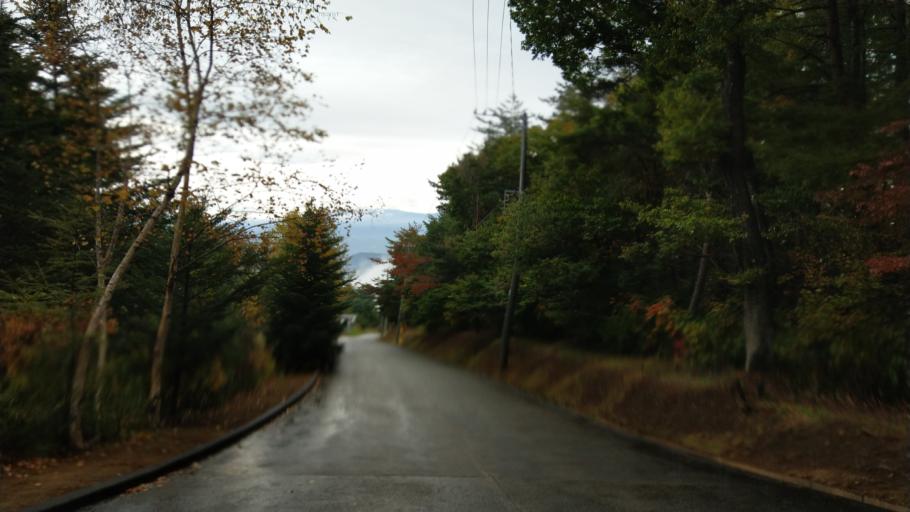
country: JP
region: Nagano
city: Komoro
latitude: 36.3661
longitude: 138.4267
